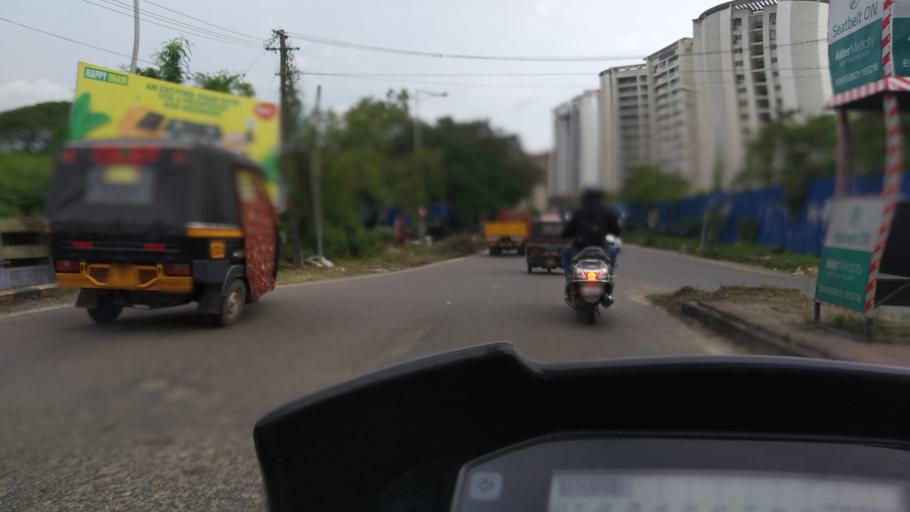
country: IN
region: Kerala
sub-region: Ernakulam
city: Cochin
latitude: 9.9919
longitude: 76.2705
